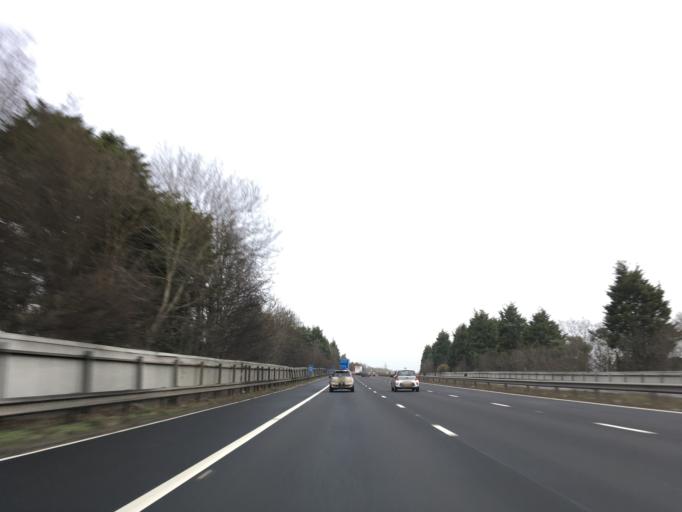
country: GB
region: England
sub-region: Gloucestershire
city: Barnwood
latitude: 51.8501
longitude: -2.1833
